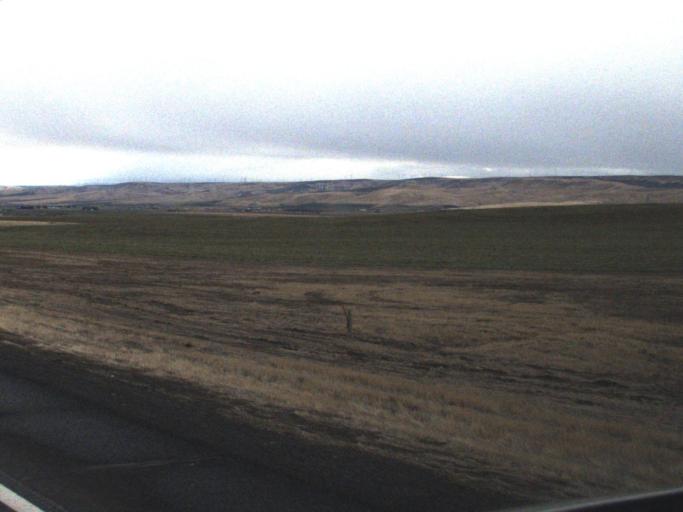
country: US
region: Washington
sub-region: Walla Walla County
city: Burbank
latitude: 46.0610
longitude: -118.7383
